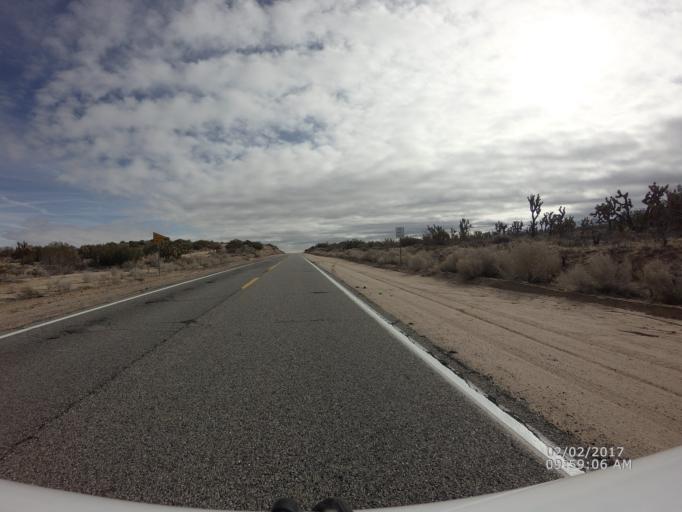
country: US
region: California
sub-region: Los Angeles County
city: Littlerock
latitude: 34.5066
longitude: -117.9864
